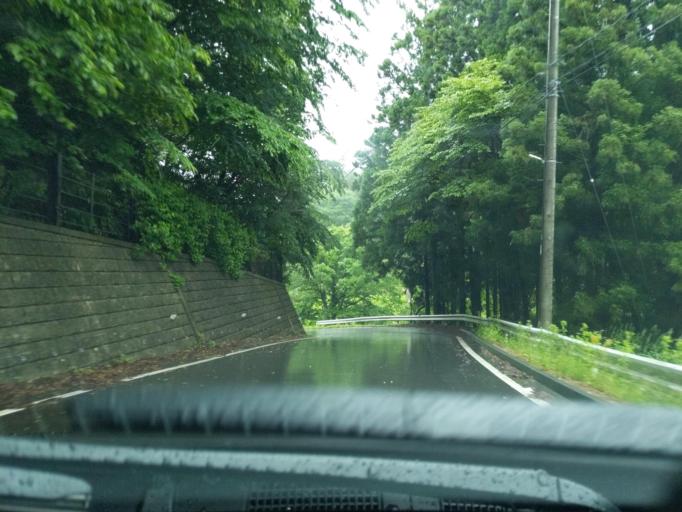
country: JP
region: Fukushima
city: Funehikimachi-funehiki
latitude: 37.6349
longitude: 140.7236
